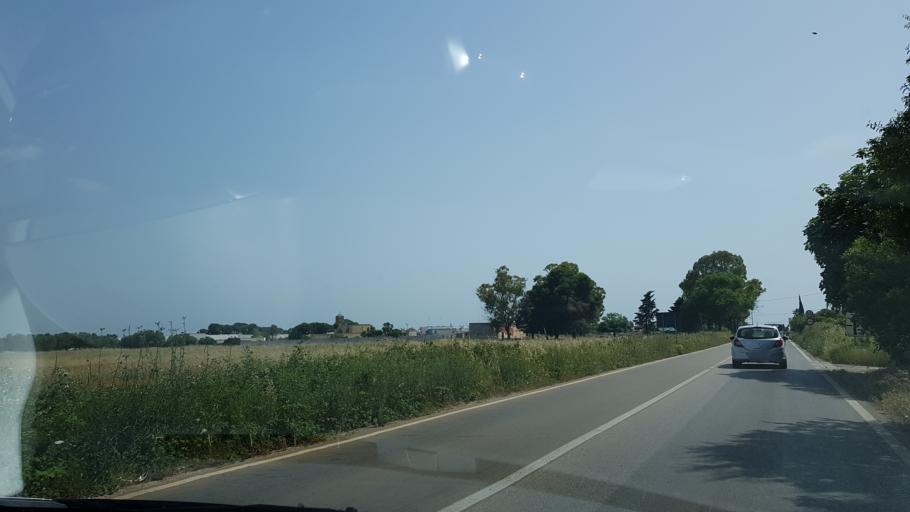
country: IT
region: Apulia
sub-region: Provincia di Lecce
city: Porto Cesareo
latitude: 40.3011
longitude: 17.8589
